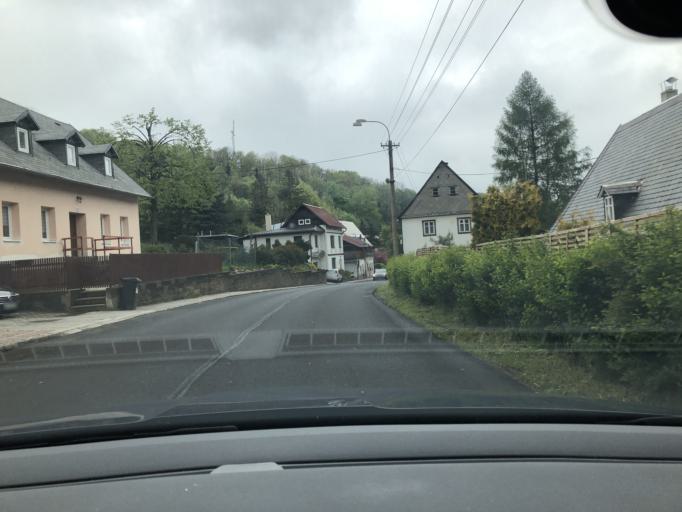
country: CZ
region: Ustecky
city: Libouchec
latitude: 50.7987
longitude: 13.9755
